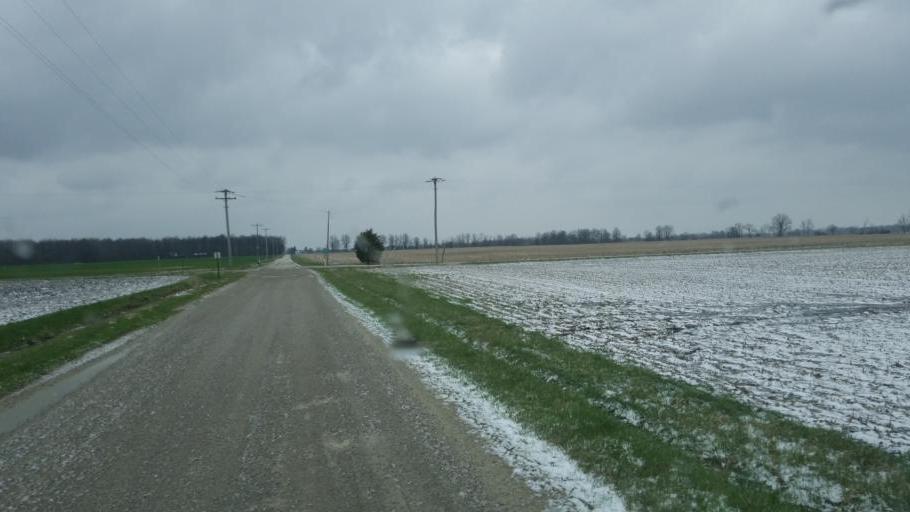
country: US
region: Ohio
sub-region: Morrow County
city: Cardington
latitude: 40.5424
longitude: -82.9338
